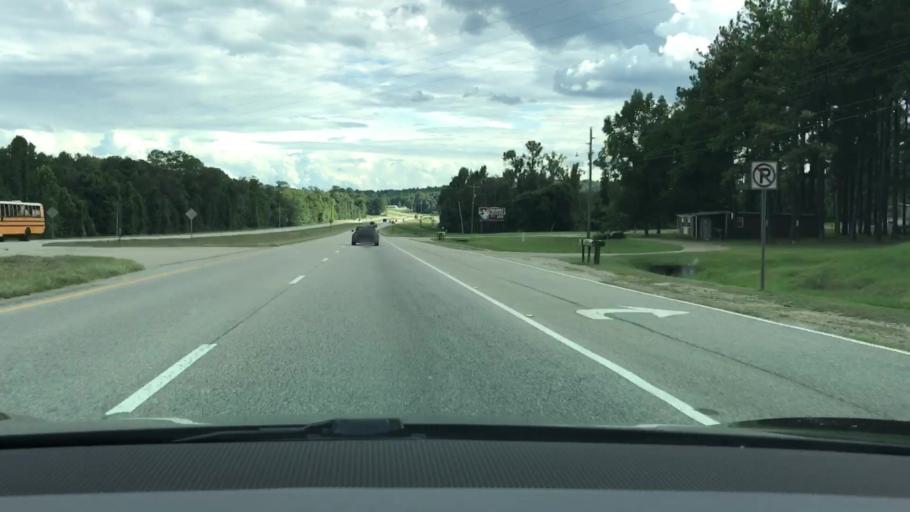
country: US
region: Alabama
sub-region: Pike County
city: Troy
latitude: 31.8517
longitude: -85.9962
